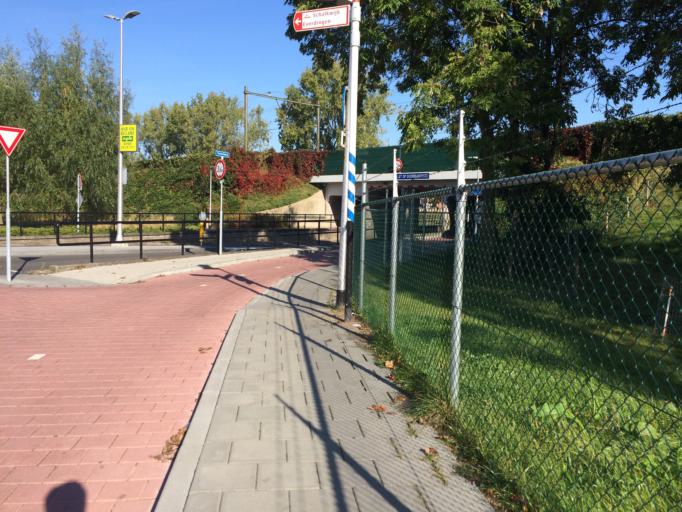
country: NL
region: Gelderland
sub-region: Gemeente Culemborg
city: Culemborg
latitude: 51.9489
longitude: 5.2242
